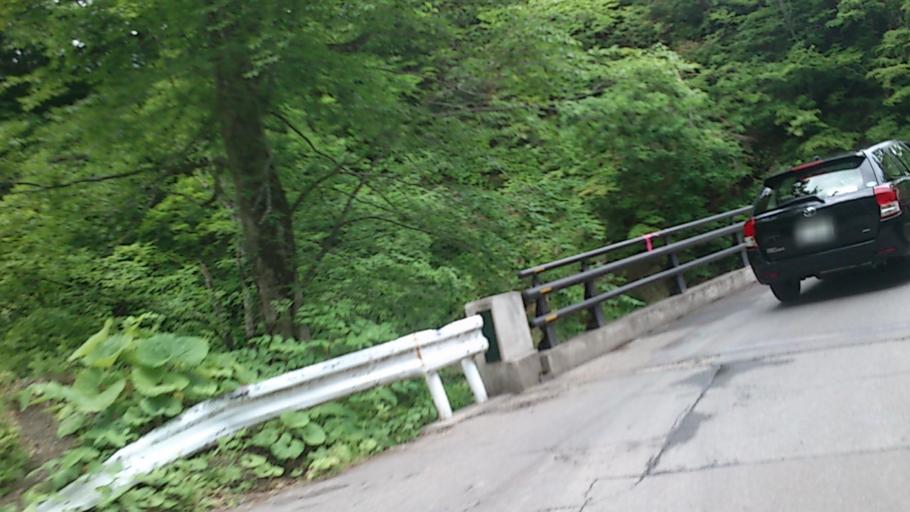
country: JP
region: Aomori
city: Hirosaki
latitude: 40.5173
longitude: 140.1861
